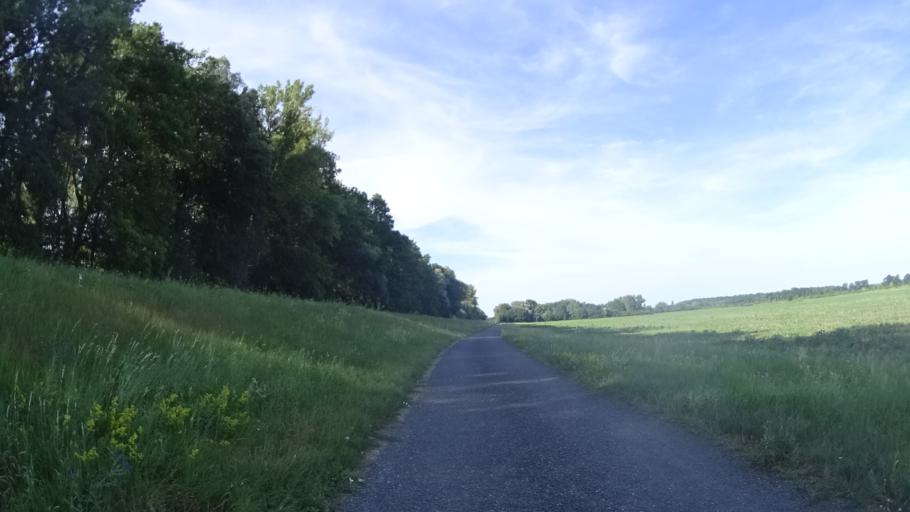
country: AT
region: Lower Austria
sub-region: Politischer Bezirk Ganserndorf
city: Drosing
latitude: 48.5393
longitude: 16.9581
